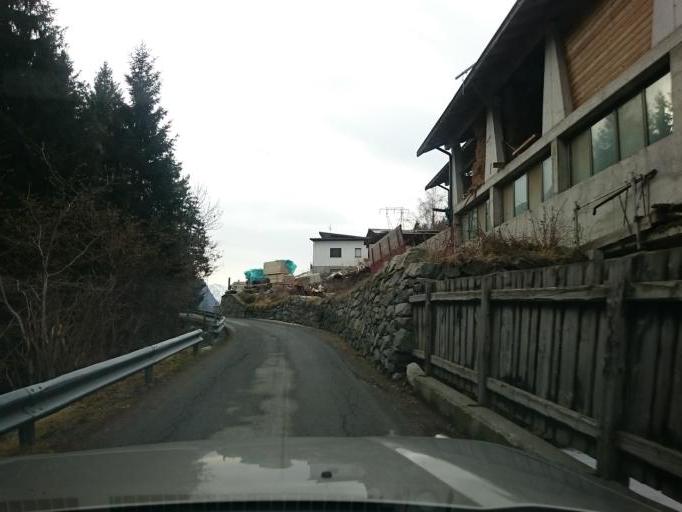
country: IT
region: Lombardy
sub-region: Provincia di Sondrio
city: Cepina
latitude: 46.4477
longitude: 10.3564
